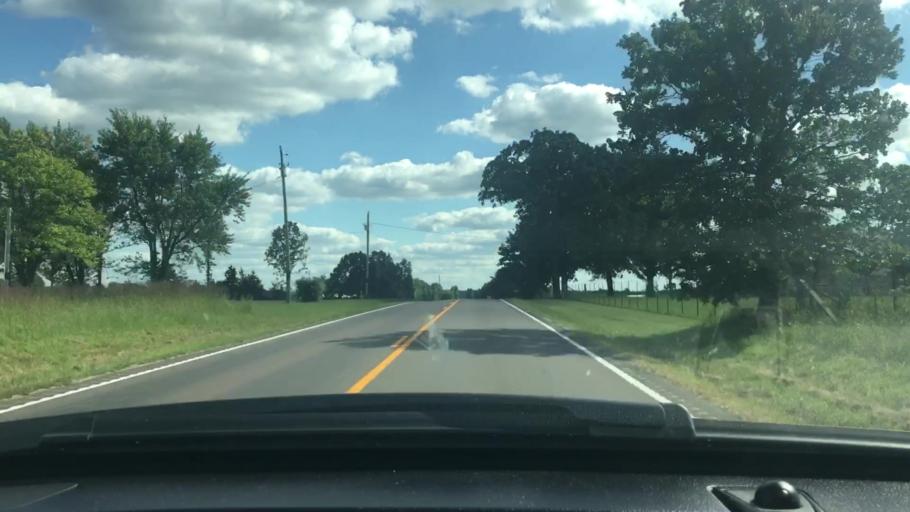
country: US
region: Missouri
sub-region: Wright County
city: Mountain Grove
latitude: 37.2631
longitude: -92.3081
